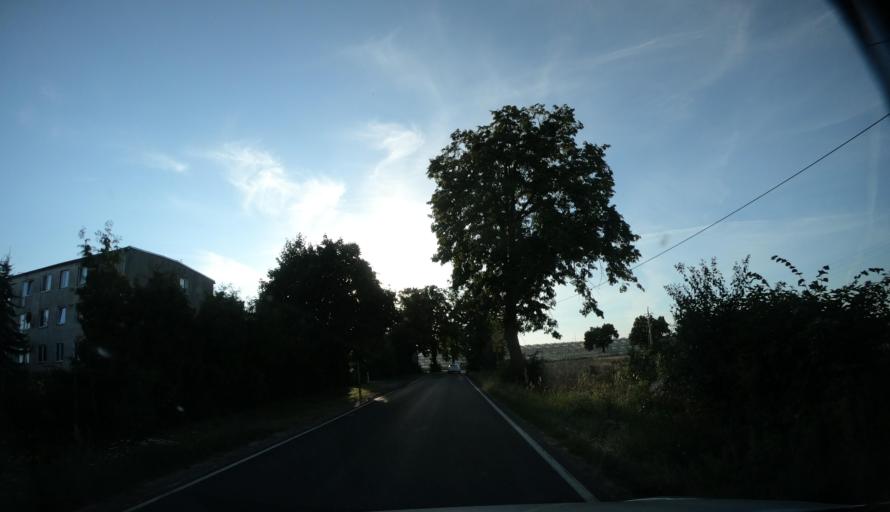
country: PL
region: Kujawsko-Pomorskie
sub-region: Powiat swiecki
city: Pruszcz
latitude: 53.2384
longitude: 18.2184
